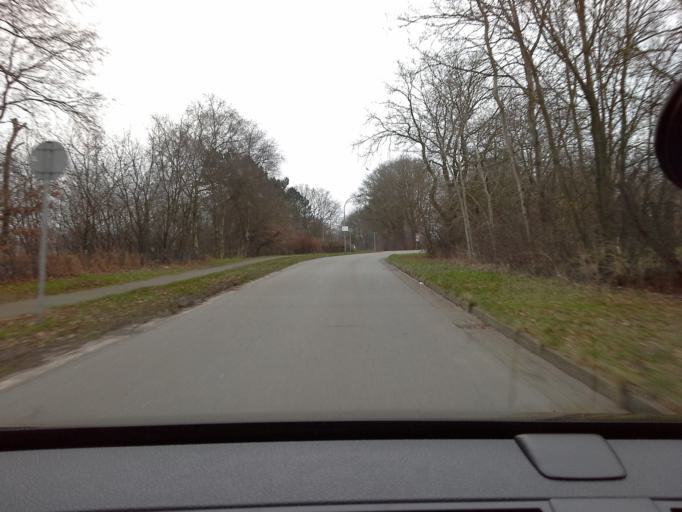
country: DE
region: Schleswig-Holstein
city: Lentfohrden
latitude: 53.8682
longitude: 9.8787
